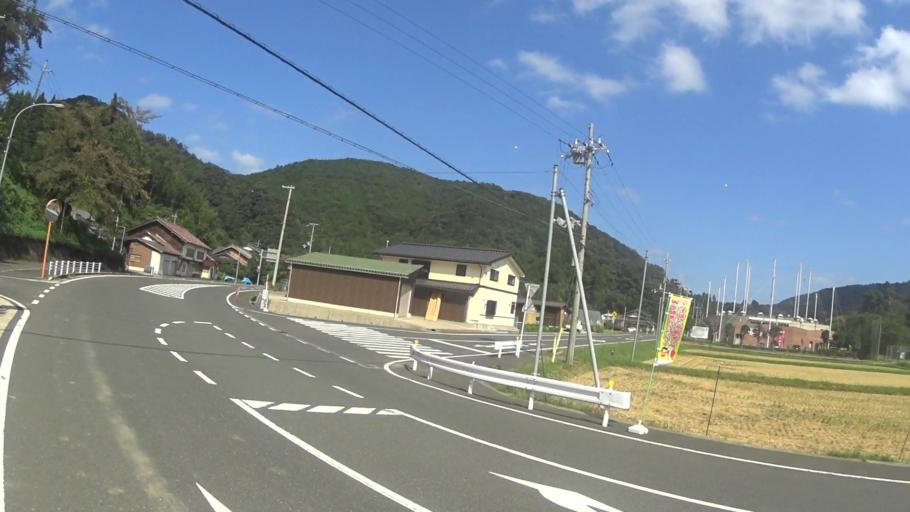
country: JP
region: Kyoto
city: Miyazu
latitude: 35.7298
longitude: 135.2557
